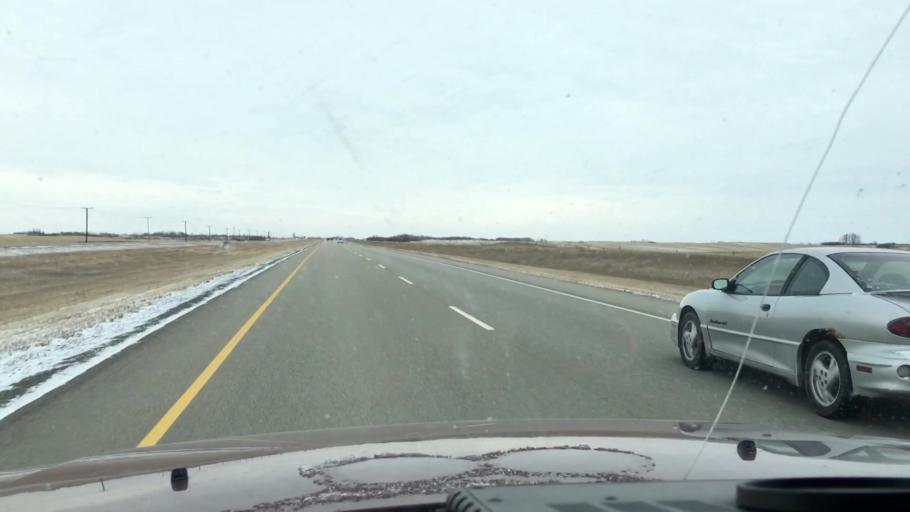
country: CA
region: Saskatchewan
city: Watrous
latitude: 51.4029
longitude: -106.1788
